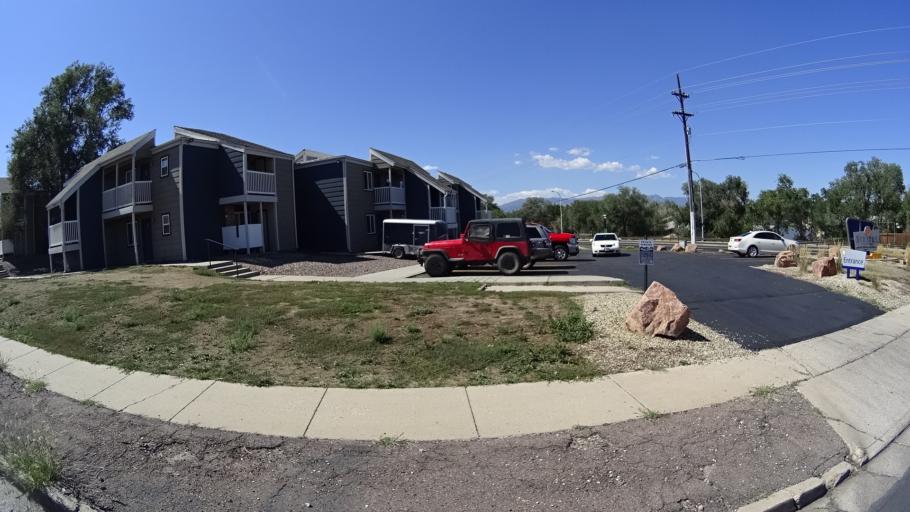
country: US
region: Colorado
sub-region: El Paso County
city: Stratmoor
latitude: 38.8250
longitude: -104.7488
